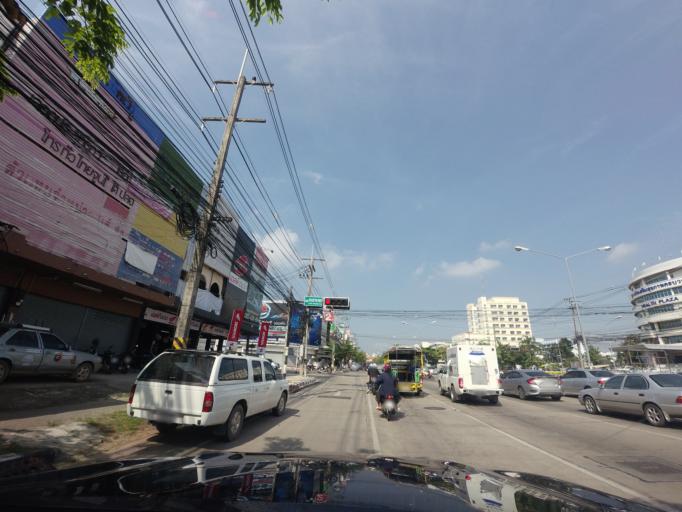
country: TH
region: Khon Kaen
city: Khon Kaen
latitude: 16.4286
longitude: 102.8518
